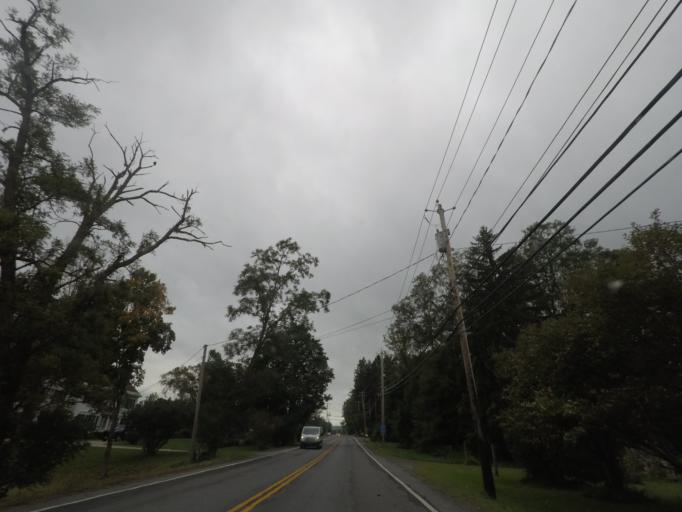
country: US
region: New York
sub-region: Rensselaer County
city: Hoosick Falls
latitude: 42.9213
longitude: -73.3490
